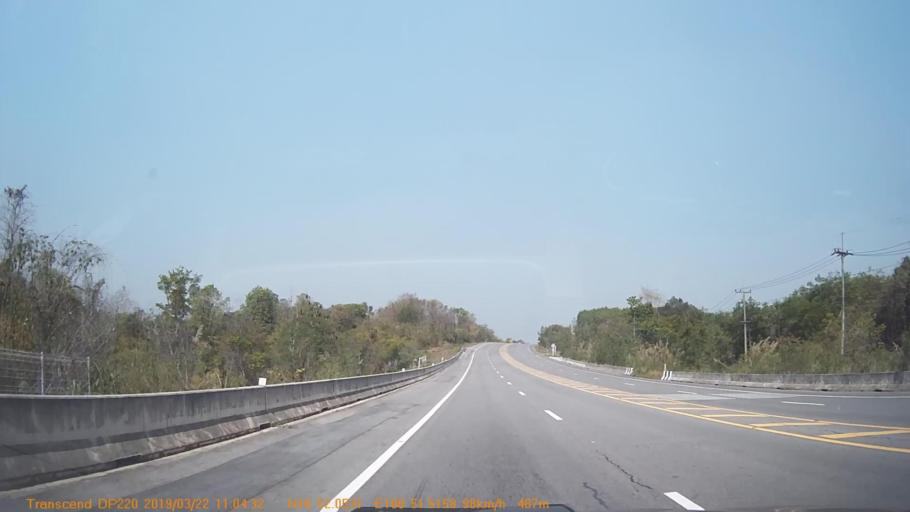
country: TH
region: Phitsanulok
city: Nakhon Thai
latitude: 16.8677
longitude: 100.8583
